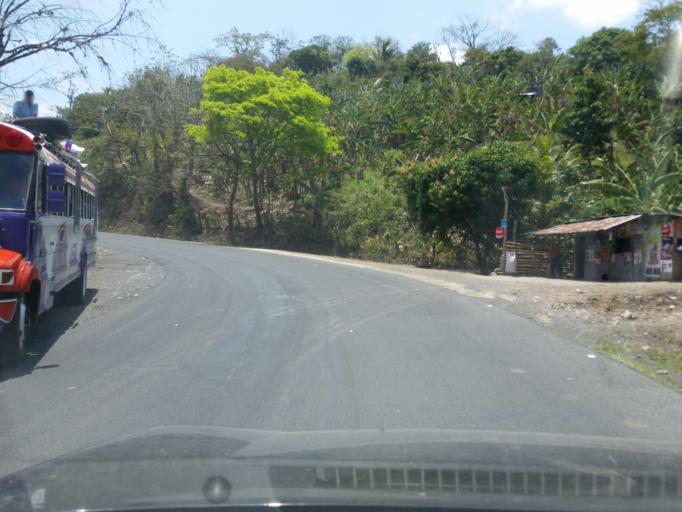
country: NI
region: Matagalpa
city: Muy Muy
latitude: 12.6085
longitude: -85.5397
